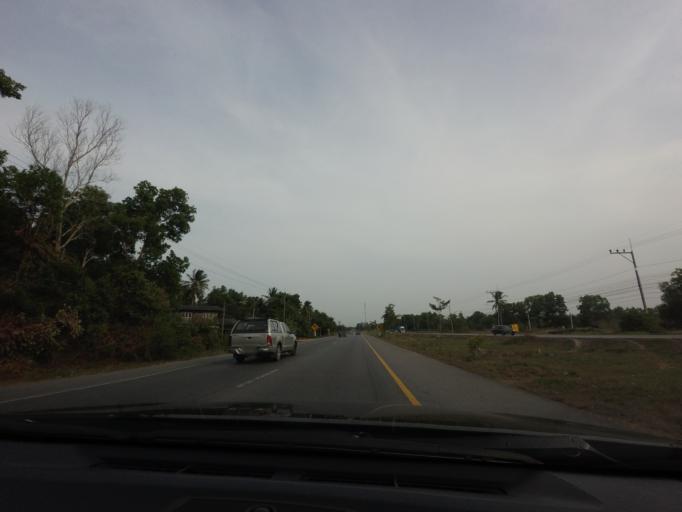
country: TH
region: Songkhla
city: Thepha
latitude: 6.9055
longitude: 100.9059
